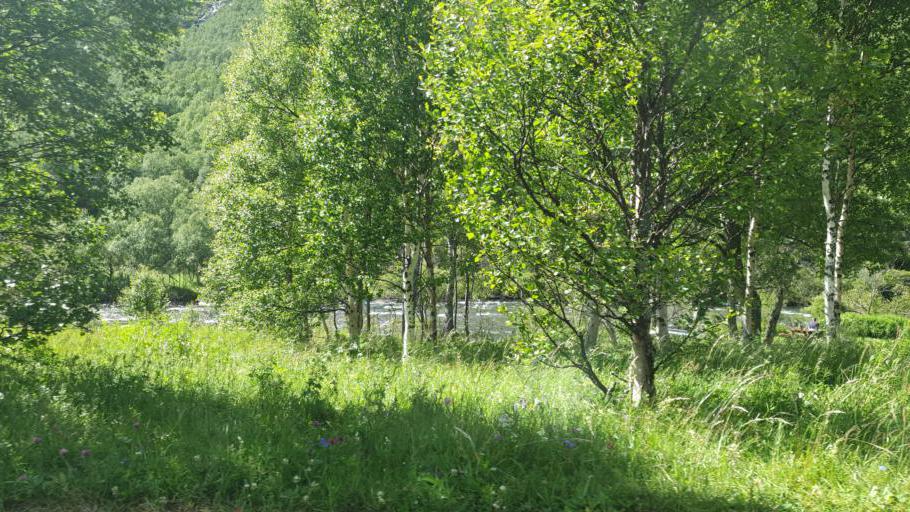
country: NO
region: Sor-Trondelag
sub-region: Oppdal
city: Oppdal
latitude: 62.4061
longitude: 9.6369
